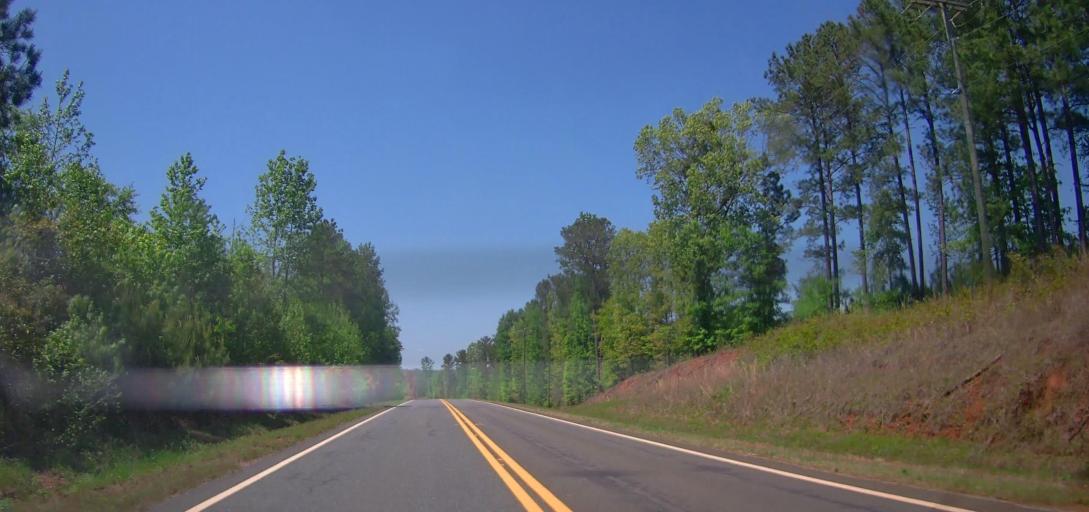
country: US
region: Georgia
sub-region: Jasper County
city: Monticello
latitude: 33.2607
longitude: -83.5731
